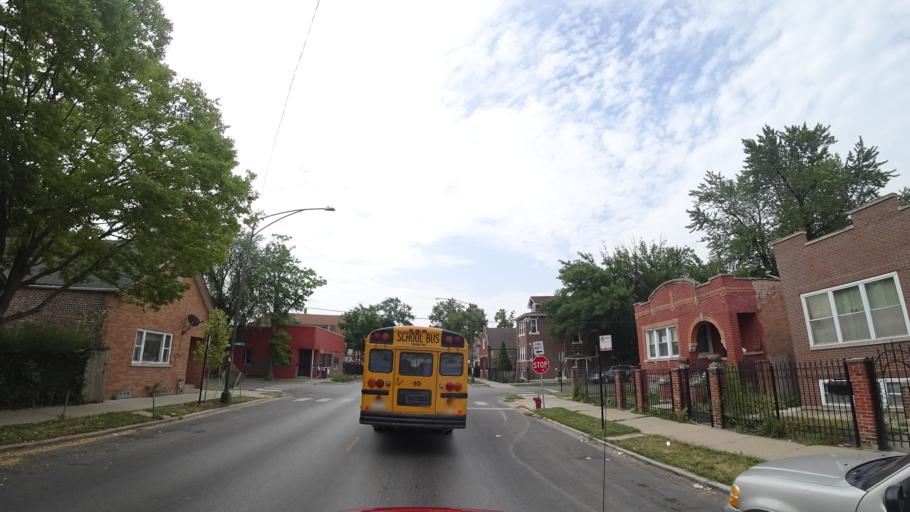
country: US
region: Illinois
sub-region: Cook County
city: Cicero
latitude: 41.8392
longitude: -87.7147
